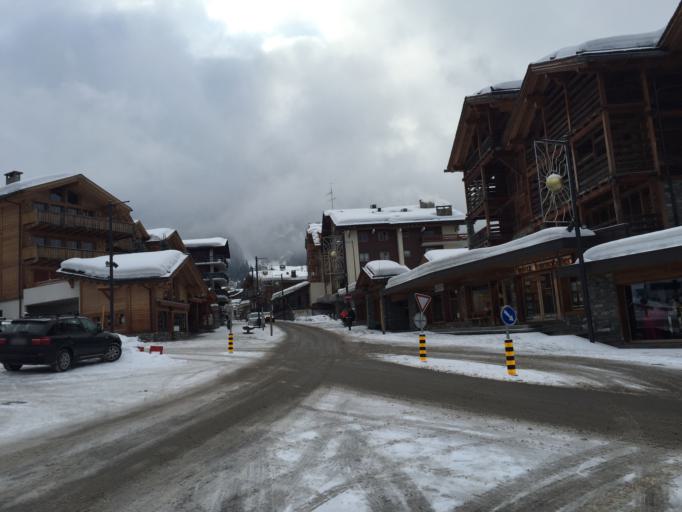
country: CH
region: Valais
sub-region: Entremont District
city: Verbier
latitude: 46.0973
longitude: 7.2252
